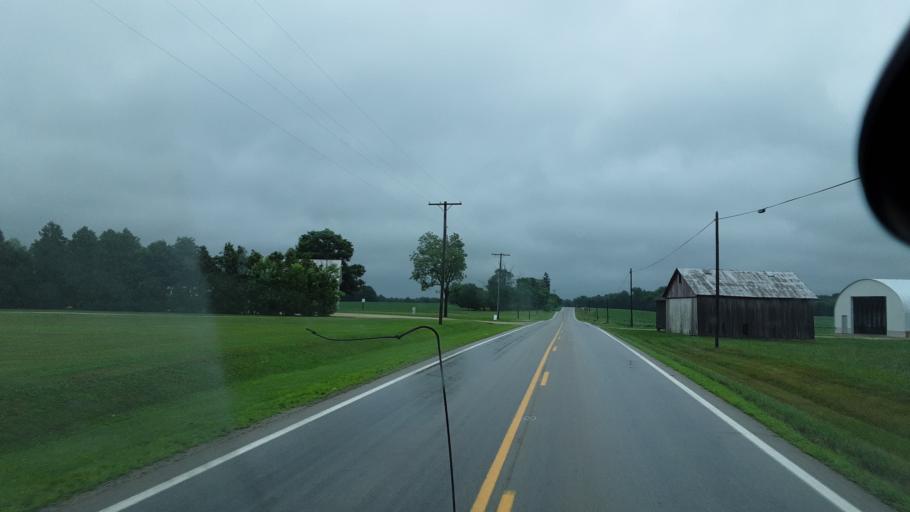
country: US
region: Ohio
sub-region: Mercer County
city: Rockford
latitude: 40.7450
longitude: -84.7598
